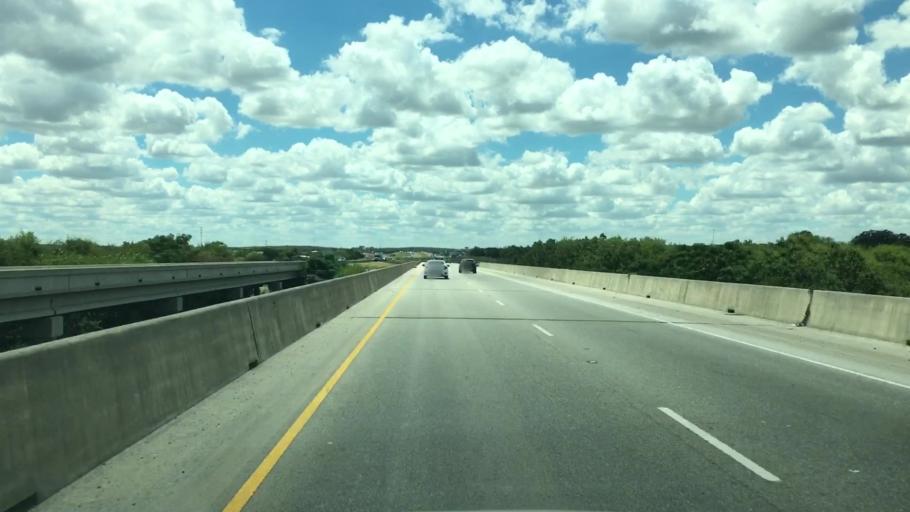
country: US
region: Texas
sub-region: Bexar County
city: Elmendorf
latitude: 29.2343
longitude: -98.4037
